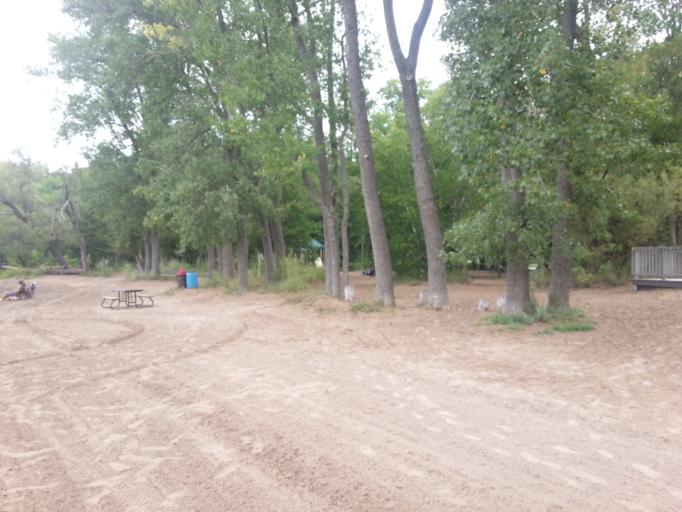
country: CA
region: Ontario
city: Prince Edward
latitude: 43.9101
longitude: -77.2736
